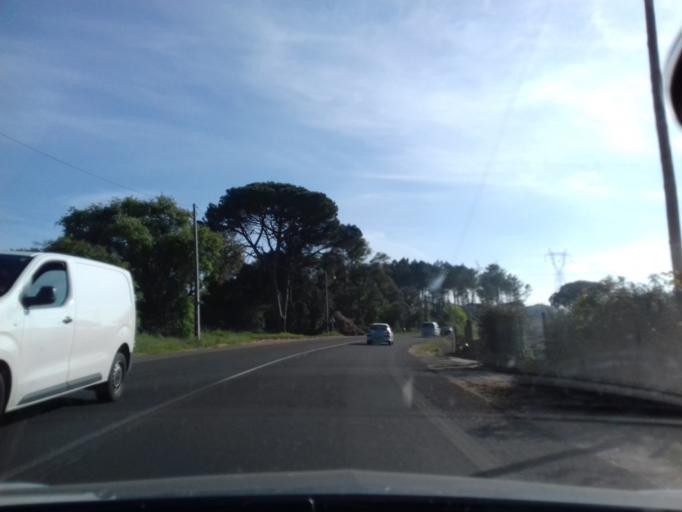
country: PT
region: Leiria
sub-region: Leiria
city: Maceira
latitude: 39.7064
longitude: -8.8625
